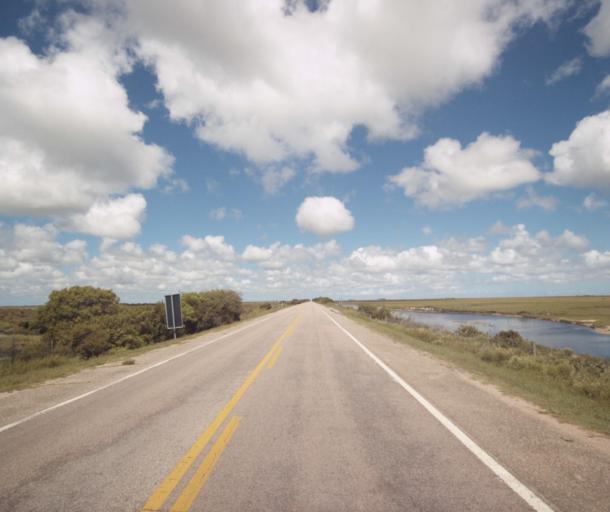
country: BR
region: Rio Grande do Sul
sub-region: Arroio Grande
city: Arroio Grande
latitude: -32.5404
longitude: -52.5395
